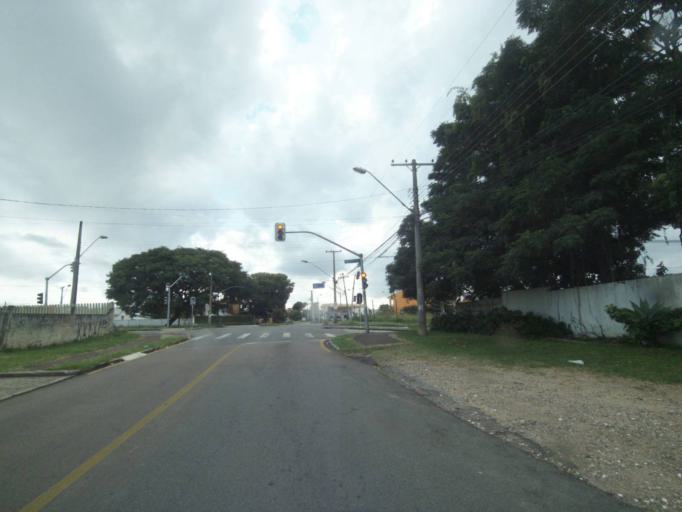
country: BR
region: Parana
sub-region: Pinhais
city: Pinhais
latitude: -25.4464
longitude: -49.2166
